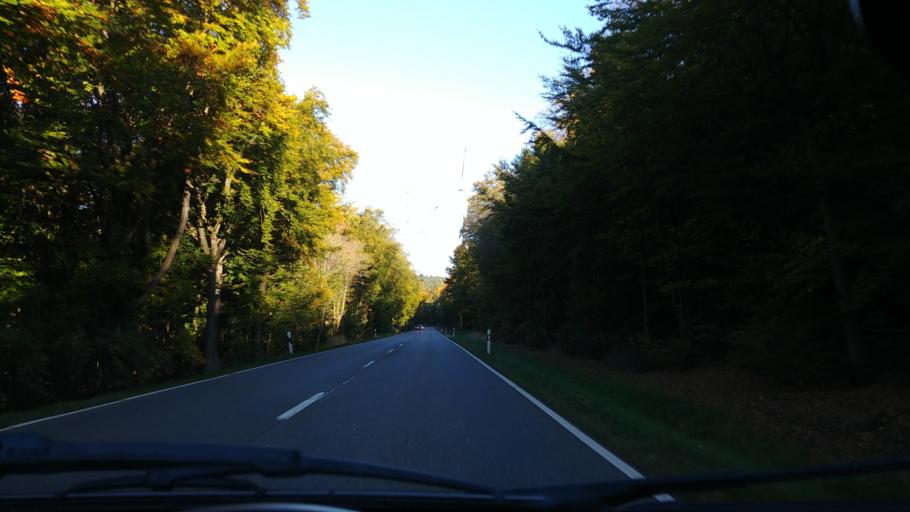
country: DE
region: Rheinland-Pfalz
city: Berndroth
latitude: 50.1957
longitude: 7.9625
